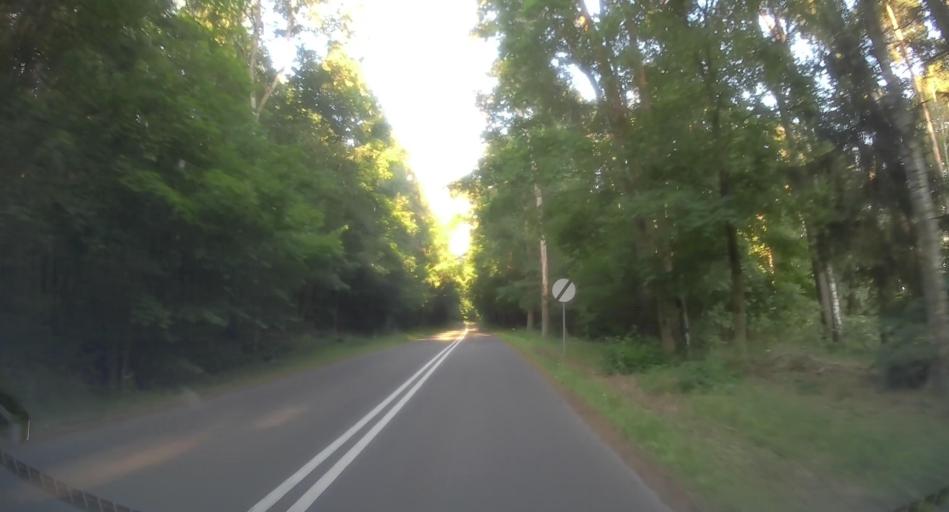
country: PL
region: Lodz Voivodeship
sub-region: Powiat skierniewicki
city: Kowiesy
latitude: 51.8920
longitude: 20.3922
